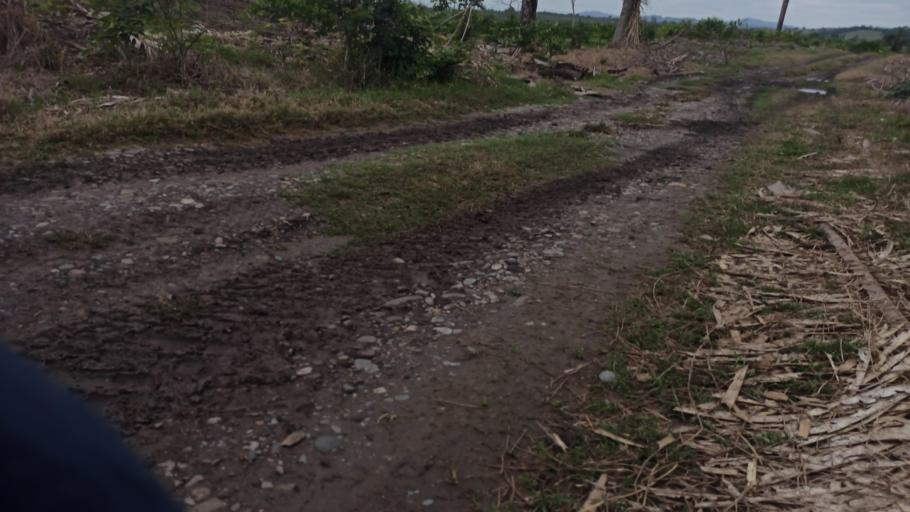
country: MX
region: Puebla
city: Espinal
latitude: 20.3004
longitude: -97.4080
